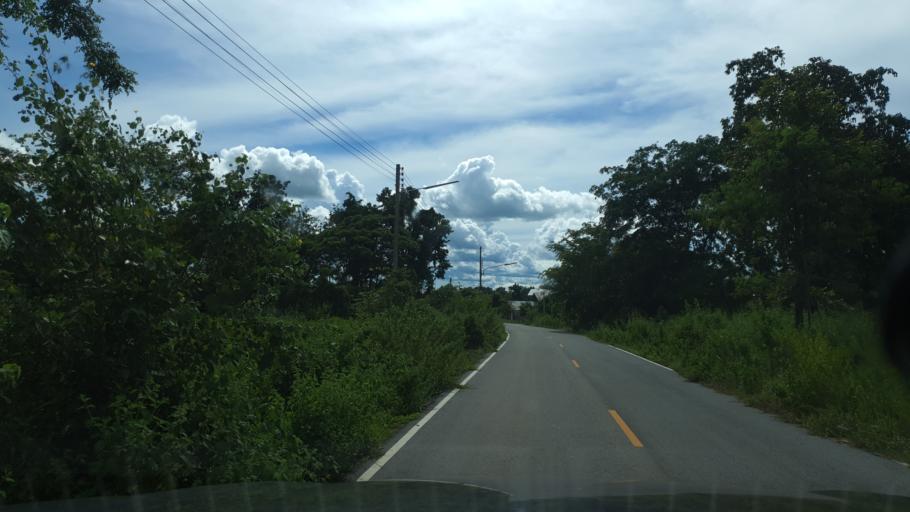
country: TH
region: Sukhothai
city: Thung Saliam
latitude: 17.3575
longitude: 99.6456
